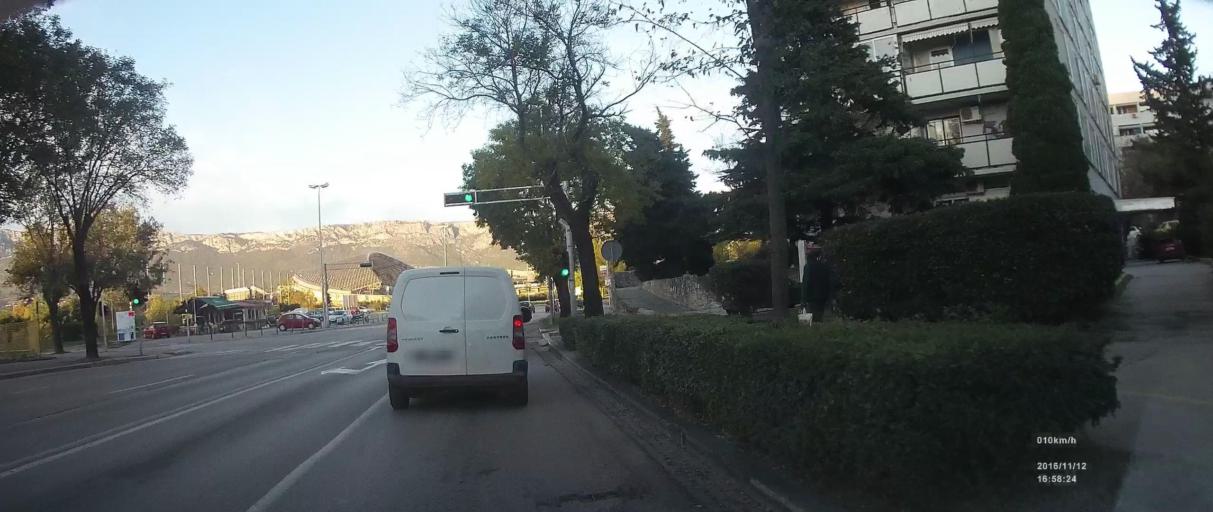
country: HR
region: Splitsko-Dalmatinska
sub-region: Grad Split
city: Split
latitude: 43.5162
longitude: 16.4298
